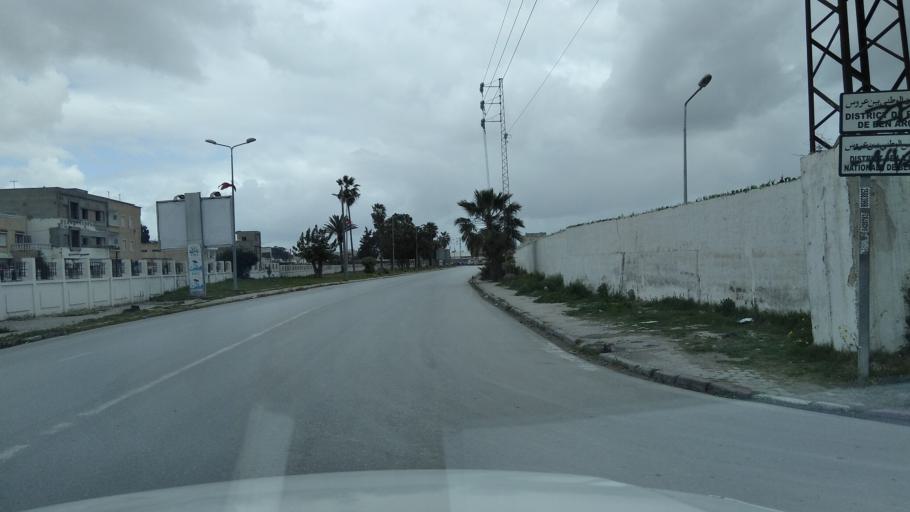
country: TN
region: Bin 'Arus
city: Ben Arous
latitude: 36.7574
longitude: 10.2187
